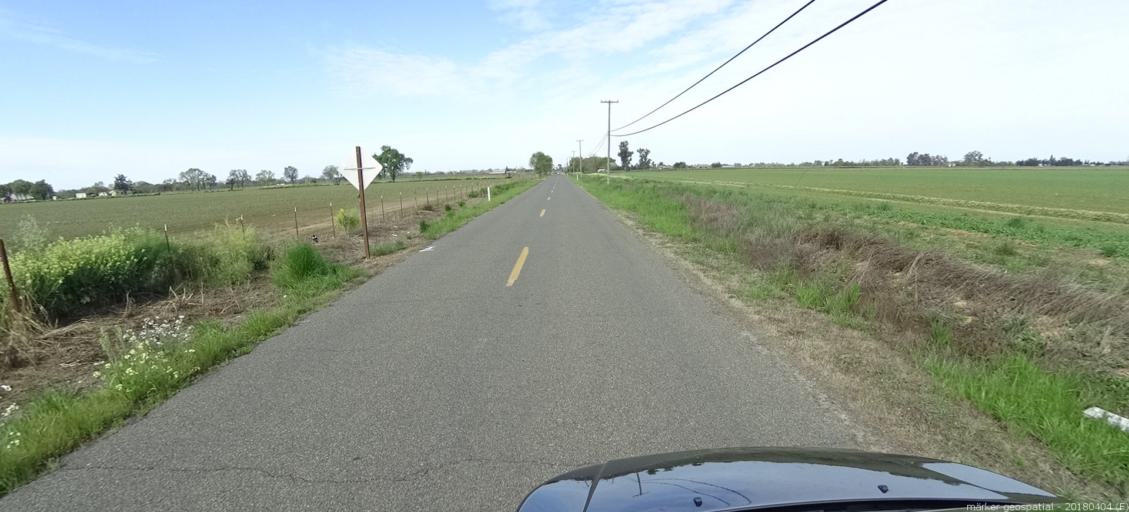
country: US
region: California
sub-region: Sacramento County
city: Herald
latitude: 38.2557
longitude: -121.2287
